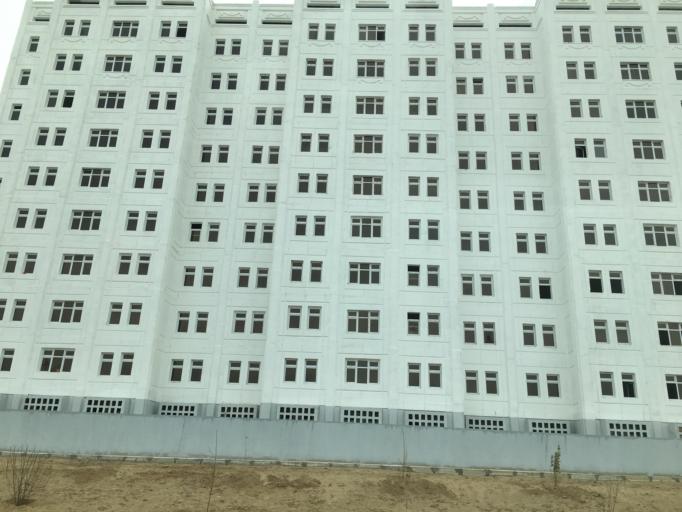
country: TM
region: Ahal
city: Ashgabat
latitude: 37.9004
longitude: 58.4124
